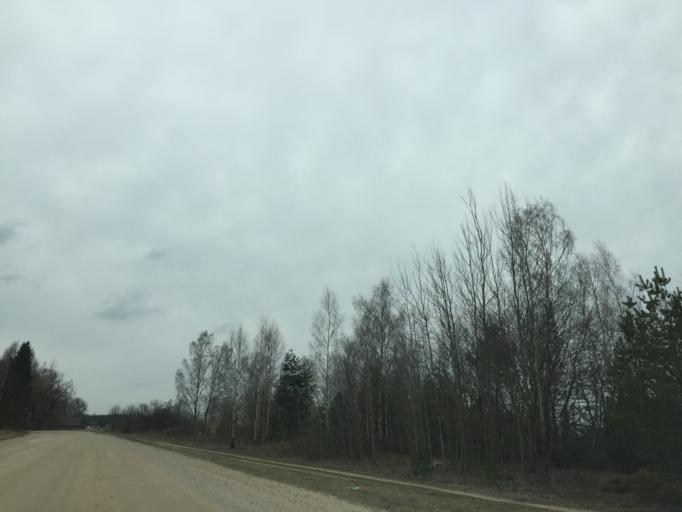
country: LV
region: Livani
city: Livani
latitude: 56.3052
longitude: 26.1696
